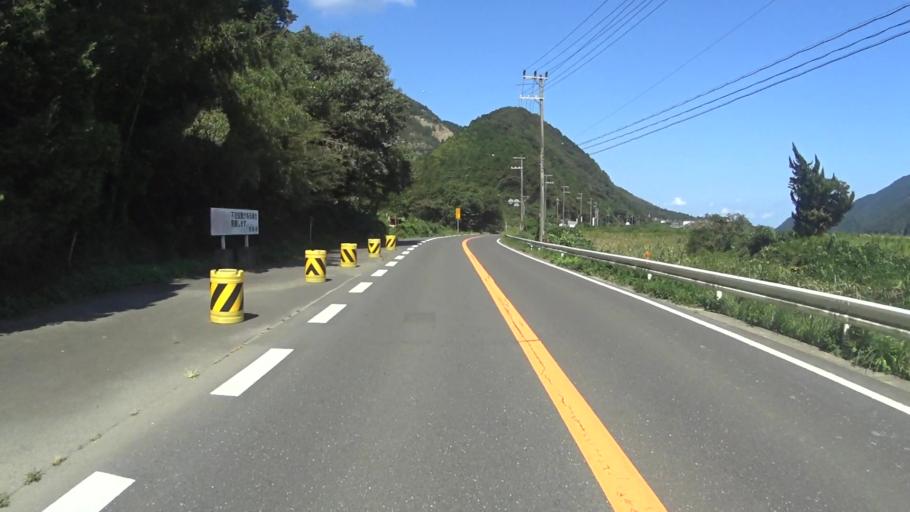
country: JP
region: Kyoto
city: Maizuru
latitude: 35.4813
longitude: 135.2782
